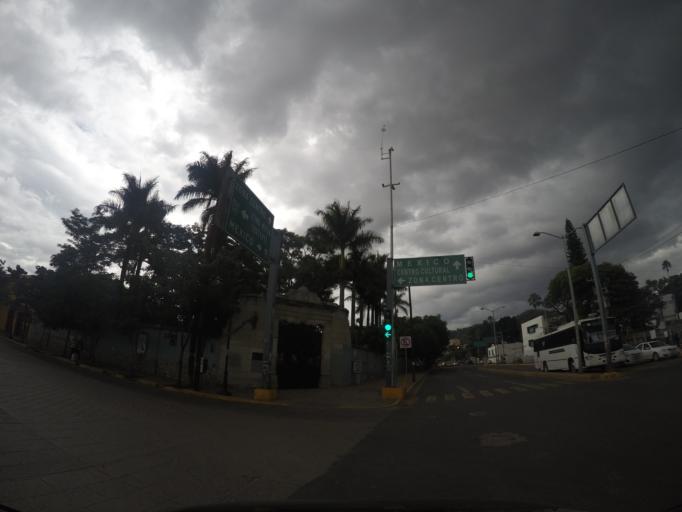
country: MX
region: Oaxaca
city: Oaxaca de Juarez
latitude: 17.0715
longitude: -96.7196
